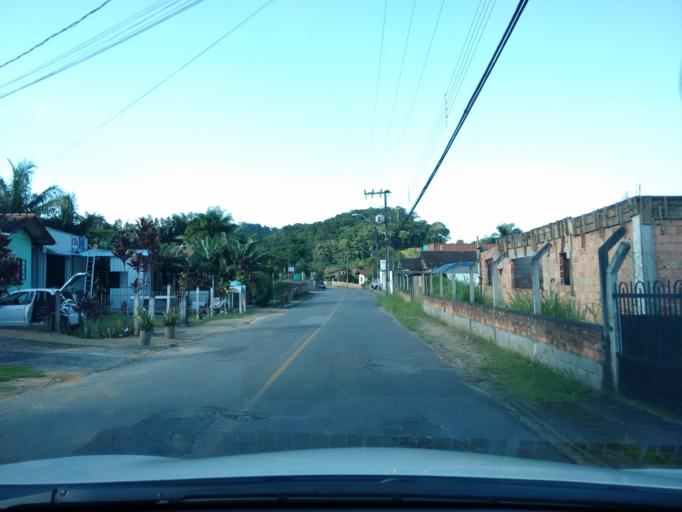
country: BR
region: Santa Catarina
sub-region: Blumenau
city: Blumenau
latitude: -26.8639
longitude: -49.0710
